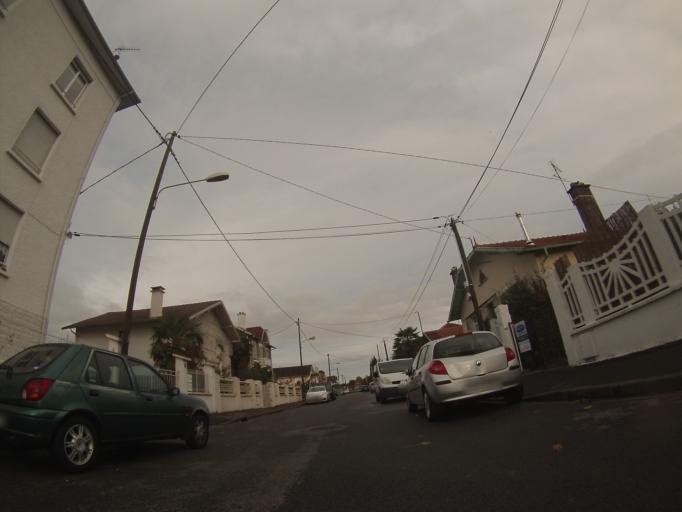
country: FR
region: Aquitaine
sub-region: Departement des Pyrenees-Atlantiques
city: Jurancon
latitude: 43.2822
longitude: -0.3844
